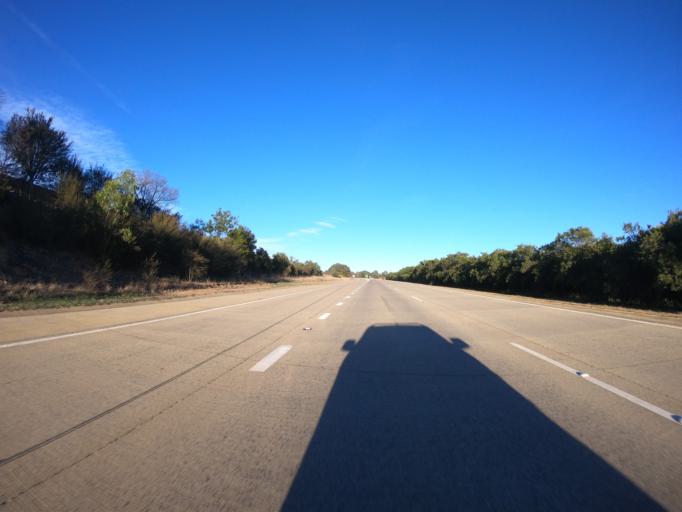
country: AU
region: New South Wales
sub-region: Yass Valley
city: Gundaroo
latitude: -35.1801
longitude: 149.2649
